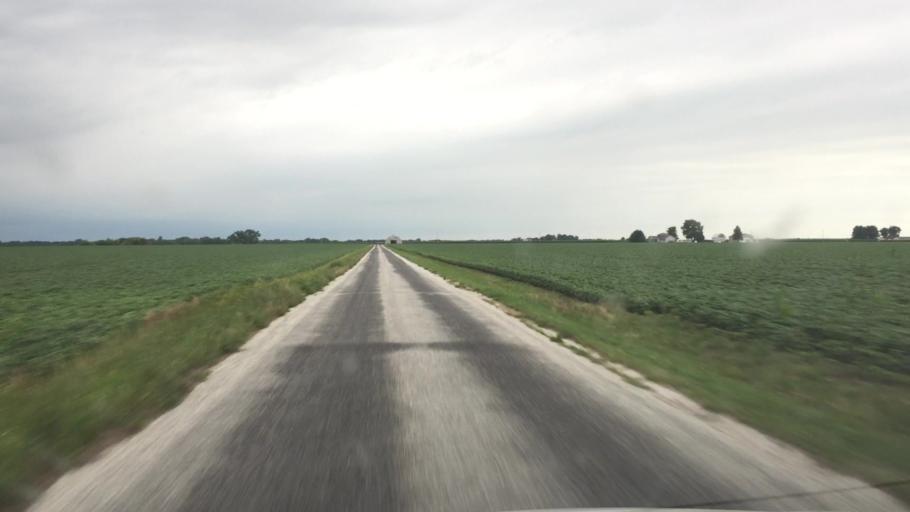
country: US
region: Illinois
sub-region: Adams County
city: Camp Point
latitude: 40.2235
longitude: -90.9691
